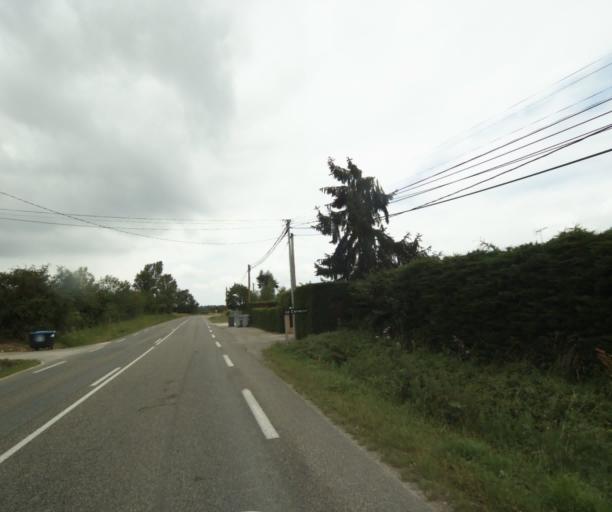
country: FR
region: Midi-Pyrenees
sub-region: Departement du Tarn-et-Garonne
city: Saint-Nauphary
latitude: 43.9781
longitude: 1.3987
